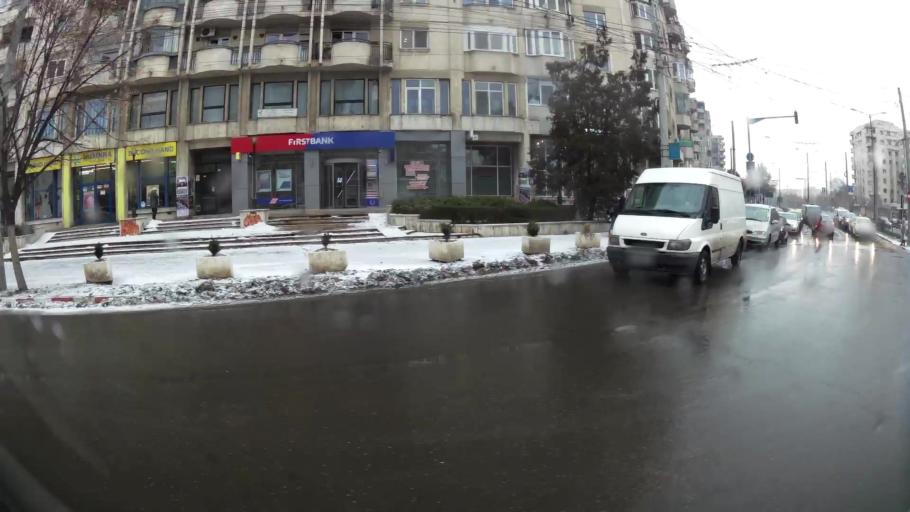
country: RO
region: Prahova
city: Ploiesti
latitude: 44.9431
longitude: 26.0177
